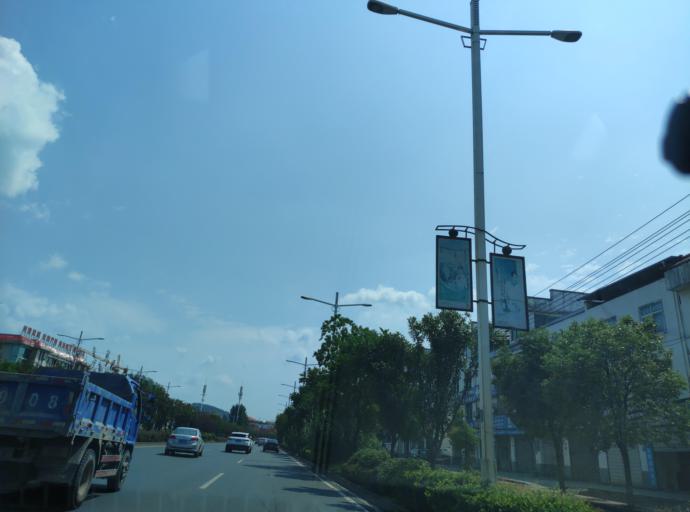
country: CN
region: Jiangxi Sheng
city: Pingxiang
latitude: 27.6572
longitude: 113.8931
